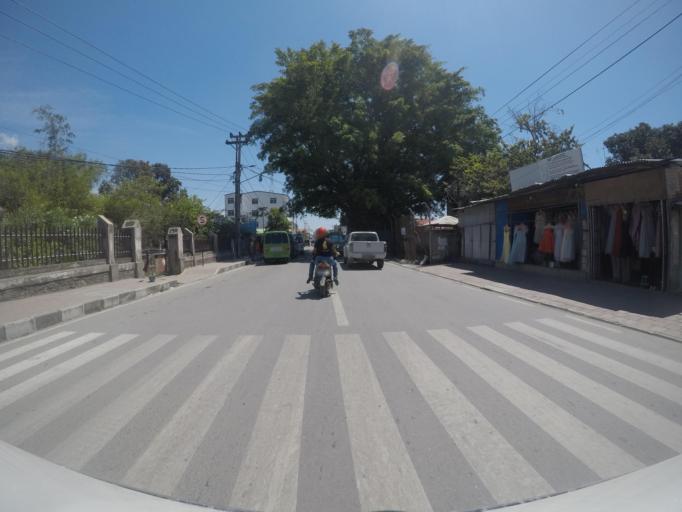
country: TL
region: Dili
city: Dili
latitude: -8.5547
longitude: 125.5911
